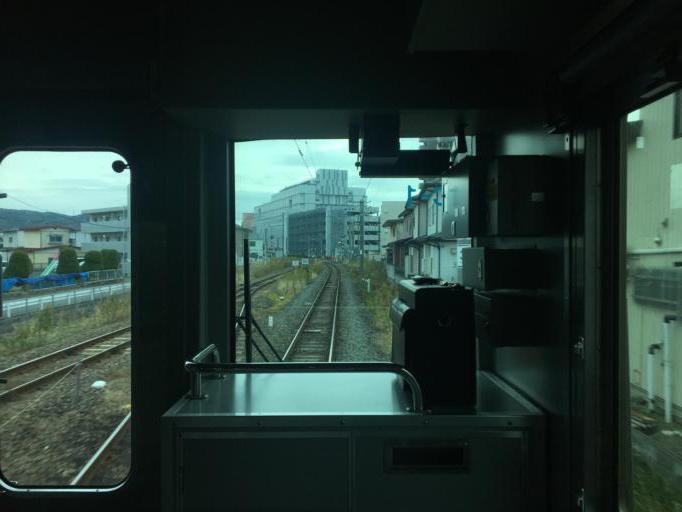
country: JP
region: Miyagi
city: Ishinomaki
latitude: 38.4365
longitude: 141.2986
